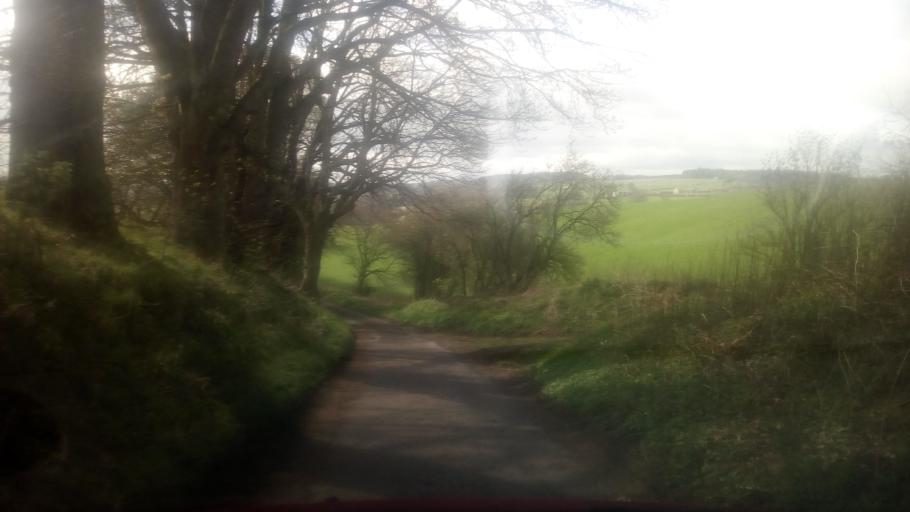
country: GB
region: Scotland
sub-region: The Scottish Borders
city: Jedburgh
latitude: 55.4943
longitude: -2.5371
